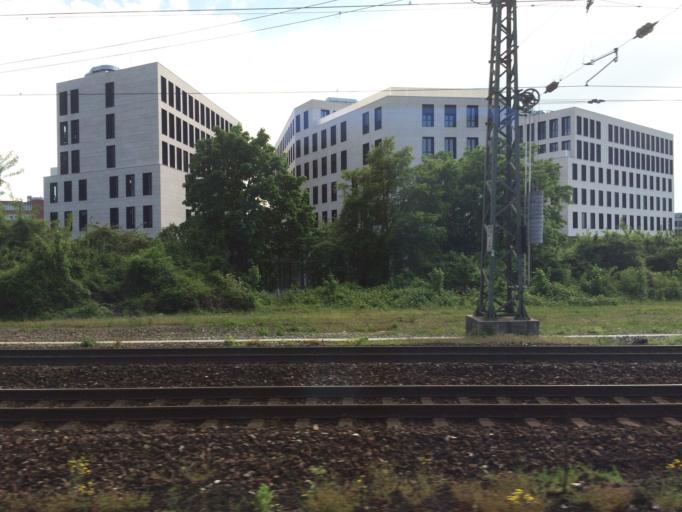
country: DE
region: Bavaria
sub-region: Regierungsbezirk Unterfranken
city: Wuerzburg
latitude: 49.8003
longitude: 9.9479
